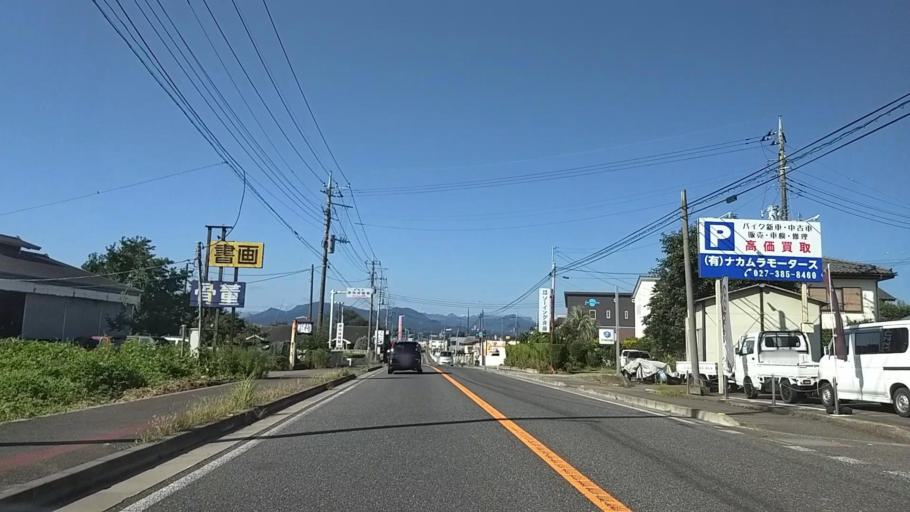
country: JP
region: Gunma
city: Annaka
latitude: 36.3121
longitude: 138.8554
